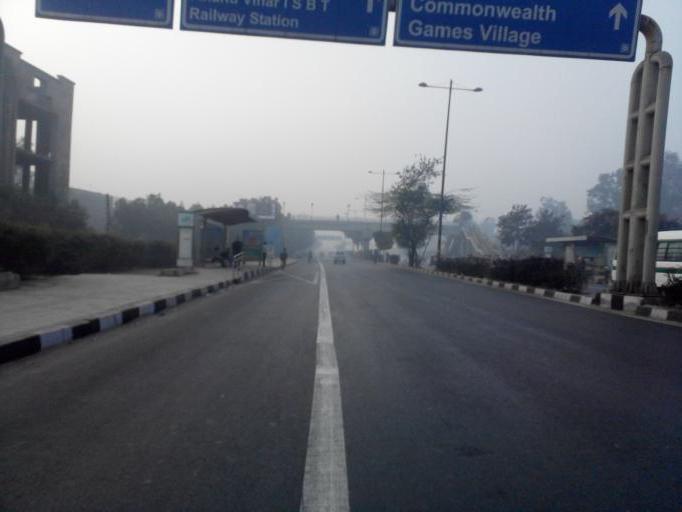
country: IN
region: Uttar Pradesh
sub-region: Gautam Buddha Nagar
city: Noida
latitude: 28.6615
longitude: 77.3203
